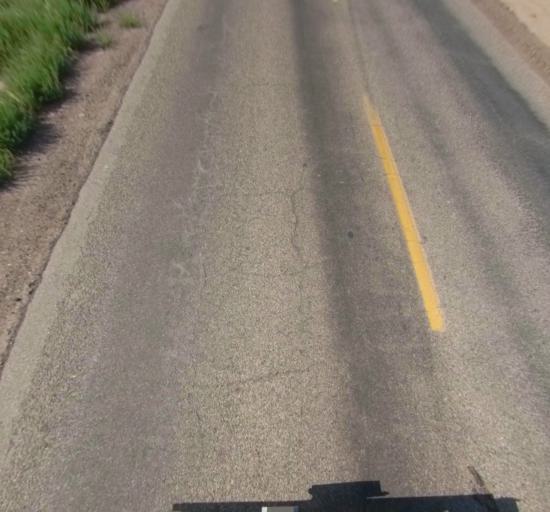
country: US
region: California
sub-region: Madera County
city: Madera
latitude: 36.9173
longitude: -120.1286
